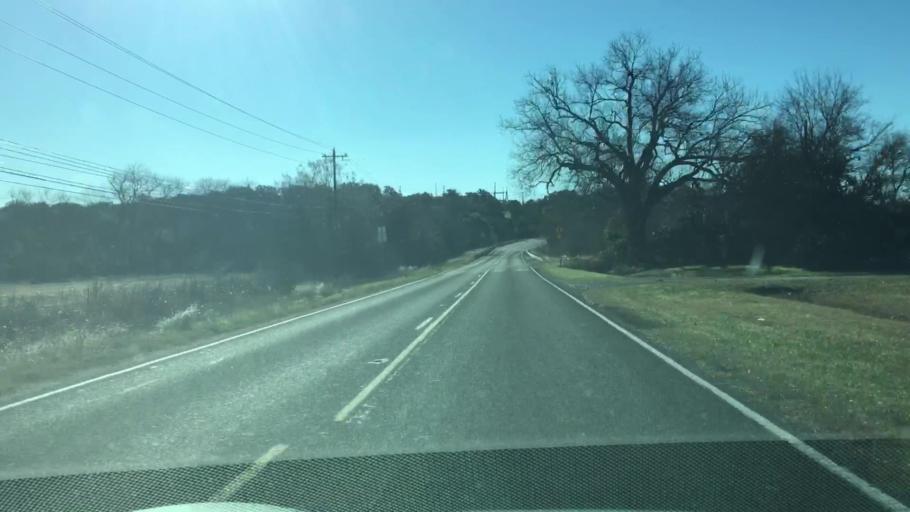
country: US
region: Texas
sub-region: Blanco County
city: Blanco
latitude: 30.0880
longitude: -98.4145
